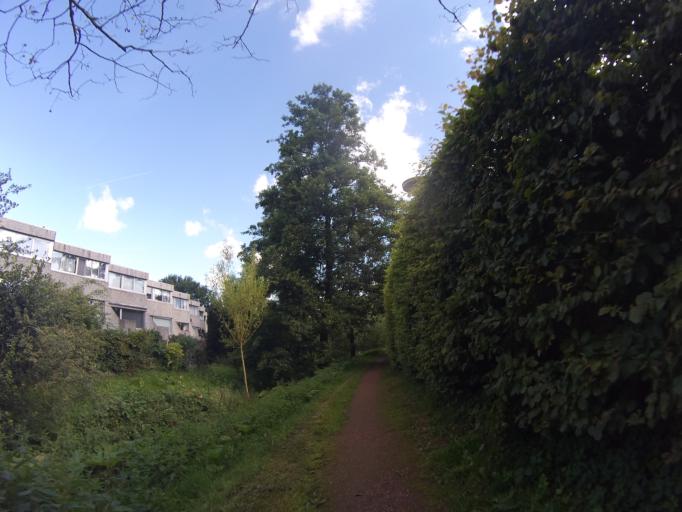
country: NL
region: Utrecht
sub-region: Gemeente Leusden
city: Leusden
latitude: 52.1333
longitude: 5.4348
